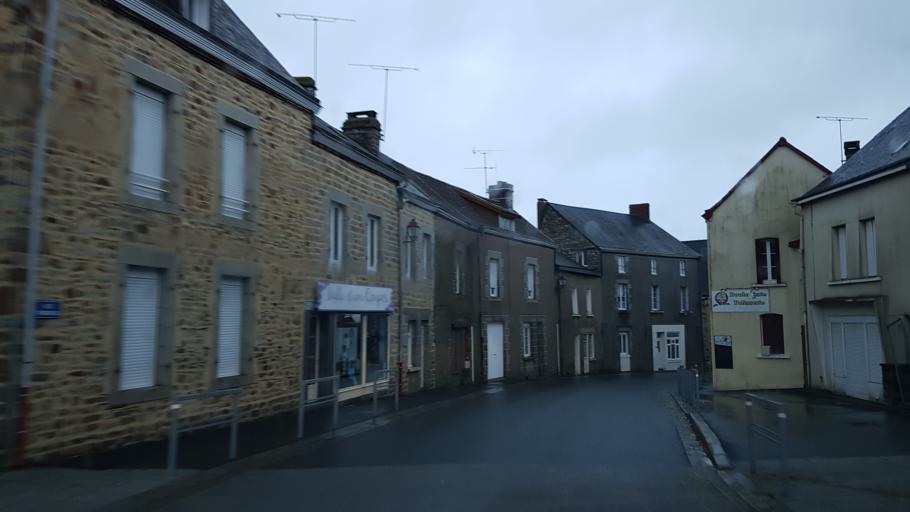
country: FR
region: Pays de la Loire
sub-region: Departement de la Mayenne
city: Juvigne
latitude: 48.2300
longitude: -1.0358
